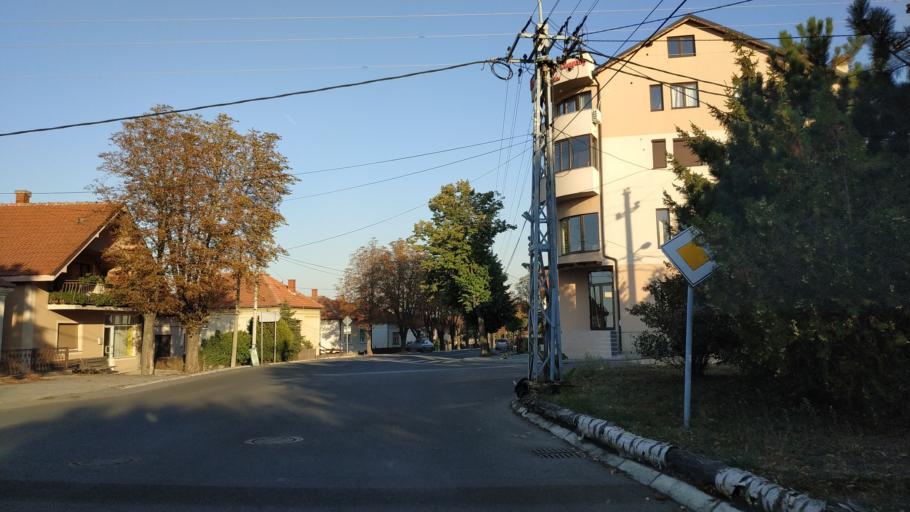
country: RS
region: Central Serbia
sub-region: Sumadijski Okrug
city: Topola
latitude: 44.2542
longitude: 20.6825
